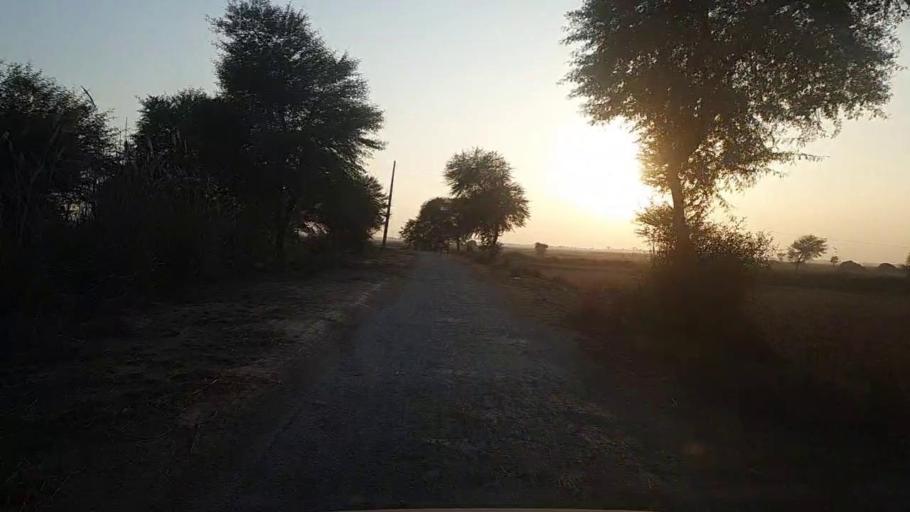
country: PK
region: Sindh
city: Khairpur Nathan Shah
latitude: 27.1809
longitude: 67.7344
